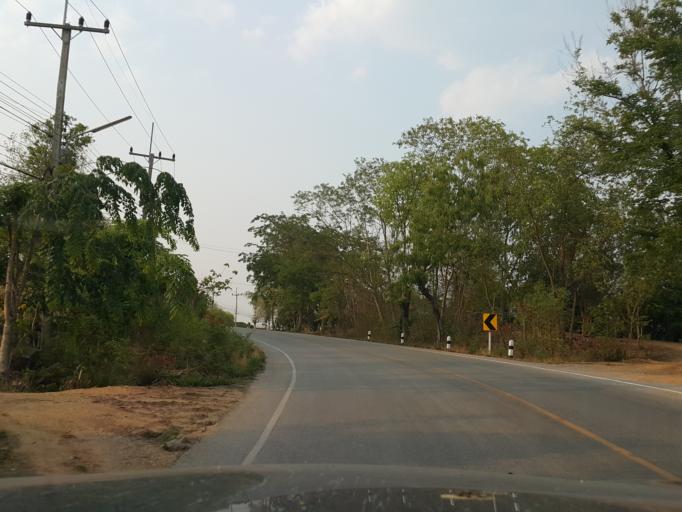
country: TH
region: Lamphun
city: Li
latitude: 17.8121
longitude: 98.9599
